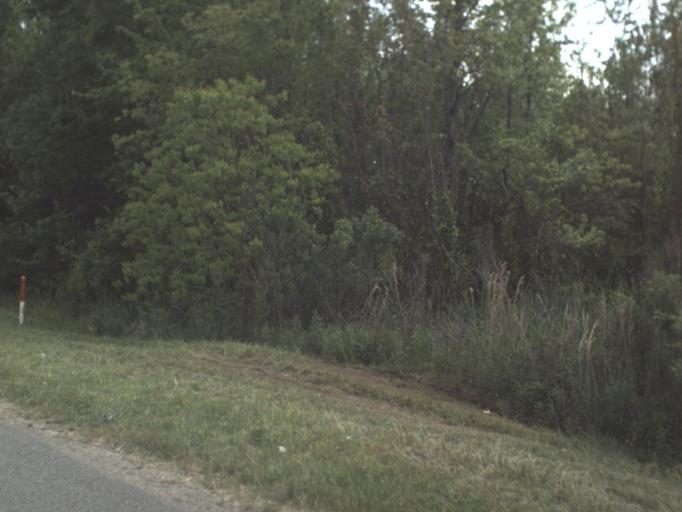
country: US
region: Florida
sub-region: Escambia County
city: Ensley
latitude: 30.5449
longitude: -87.2821
